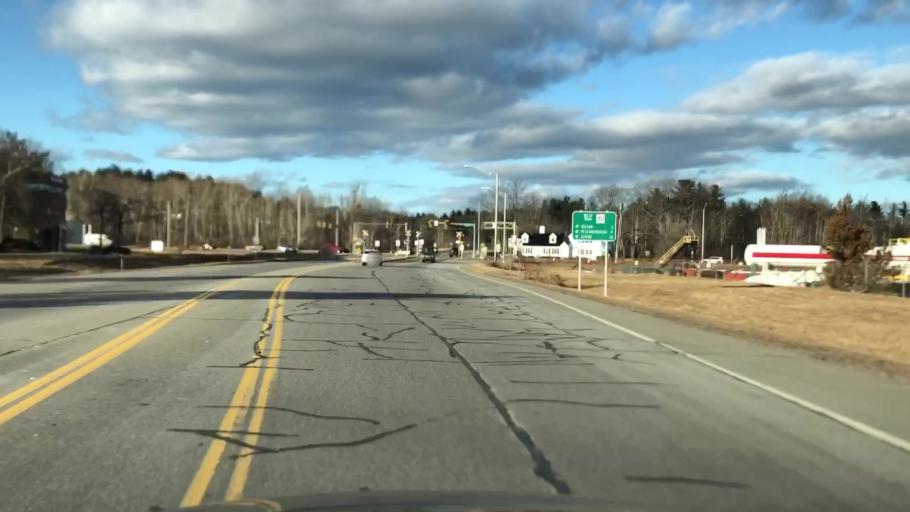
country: US
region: New Hampshire
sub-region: Hillsborough County
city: Wilton
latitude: 42.8408
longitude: -71.7030
